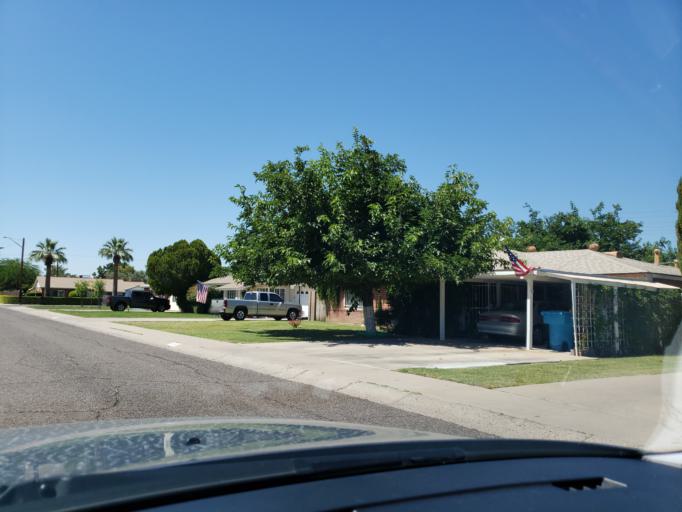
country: US
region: Arizona
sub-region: Maricopa County
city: Phoenix
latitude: 33.5183
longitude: -112.0868
